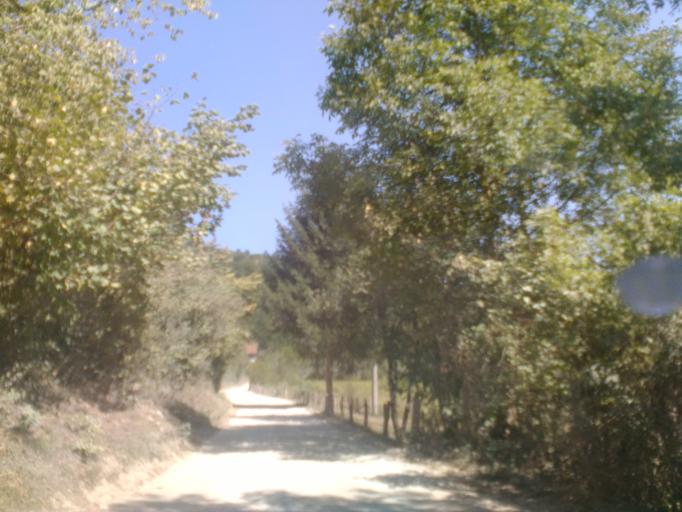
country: BA
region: Federation of Bosnia and Herzegovina
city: Orasac
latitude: 44.6225
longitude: 16.0566
